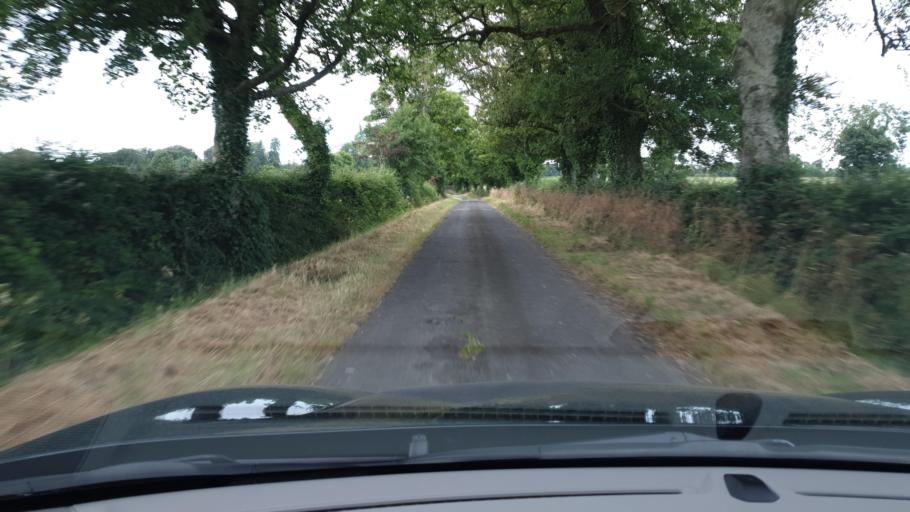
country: IE
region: Leinster
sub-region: An Mhi
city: Ashbourne
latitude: 53.5467
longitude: -6.3871
